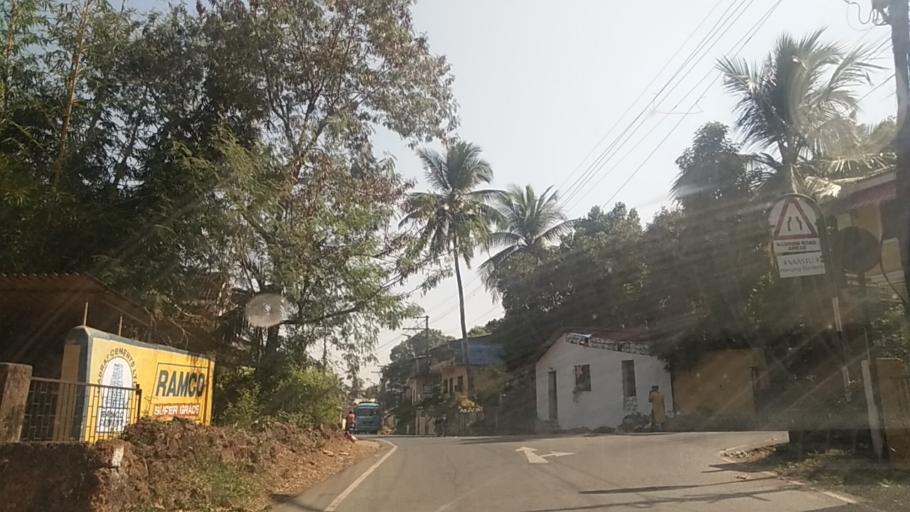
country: IN
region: Goa
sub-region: North Goa
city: Panaji
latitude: 15.5055
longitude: 73.8661
